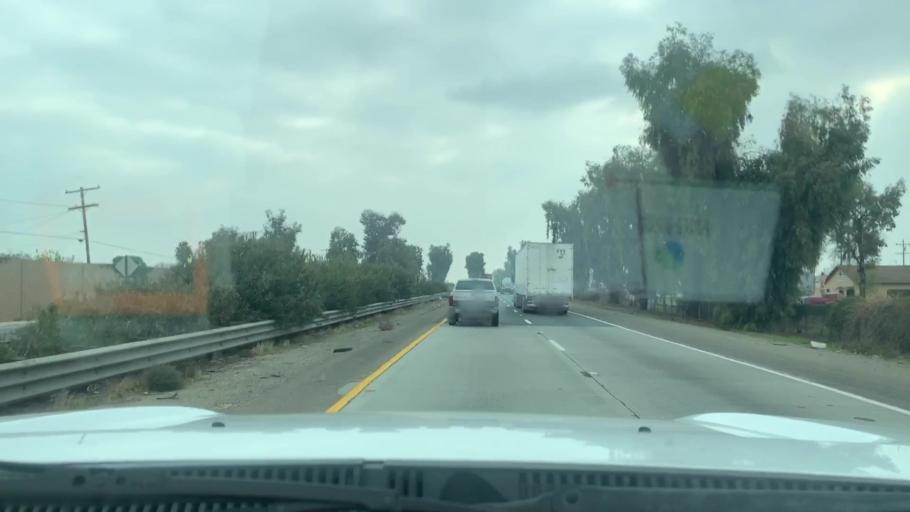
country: US
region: California
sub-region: Tulare County
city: Tipton
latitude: 36.0579
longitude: -119.3119
